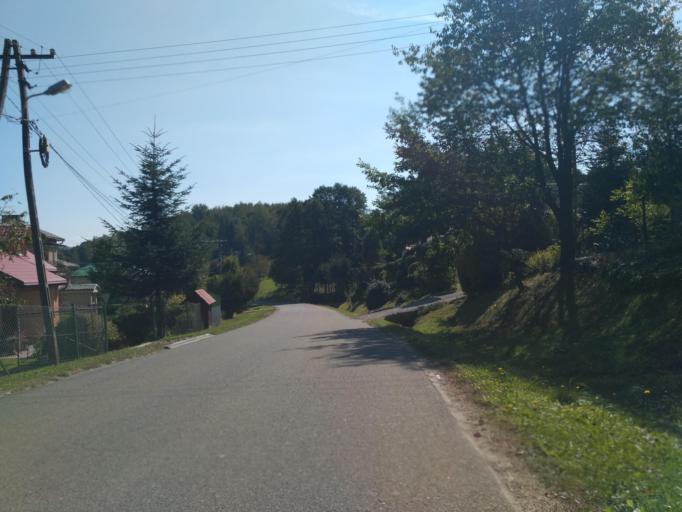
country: PL
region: Subcarpathian Voivodeship
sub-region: Powiat brzozowski
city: Niebocko
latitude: 49.6625
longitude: 22.1215
